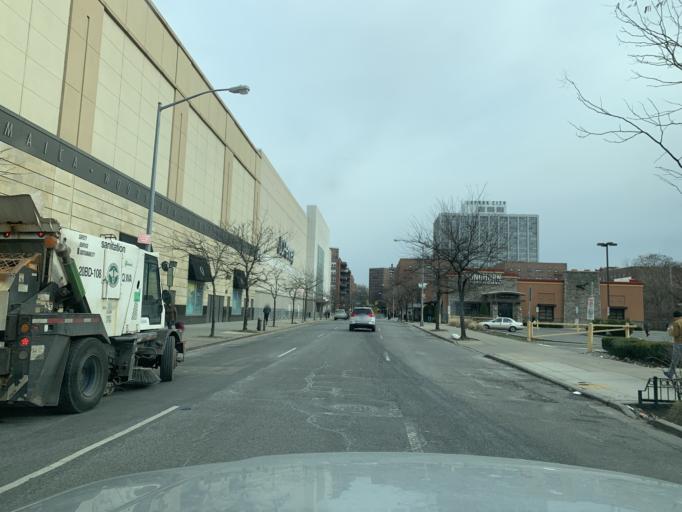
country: US
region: New York
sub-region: Queens County
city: Borough of Queens
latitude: 40.7342
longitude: -73.8689
